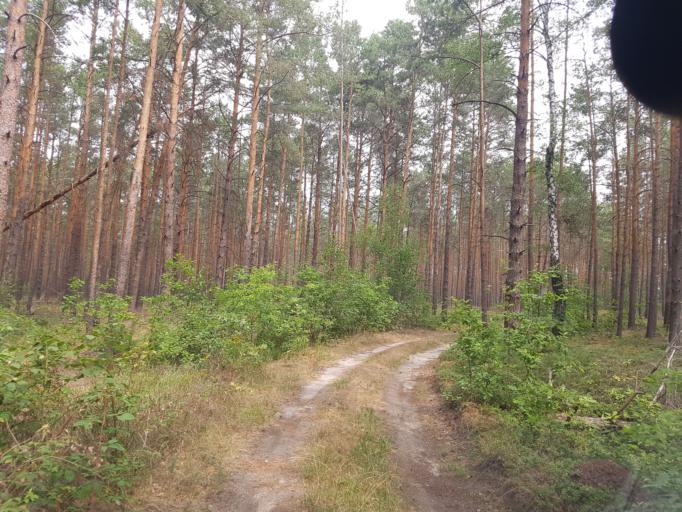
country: DE
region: Brandenburg
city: Finsterwalde
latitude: 51.6503
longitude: 13.6752
